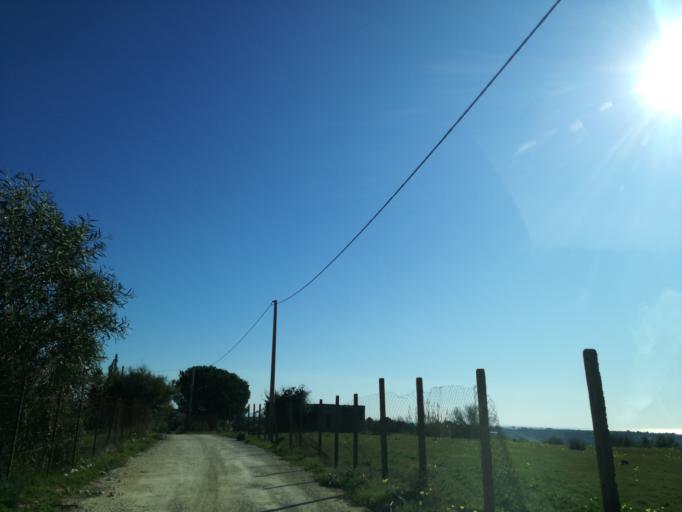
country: IT
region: Sicily
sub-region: Provincia di Caltanissetta
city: Niscemi
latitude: 37.0578
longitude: 14.3590
